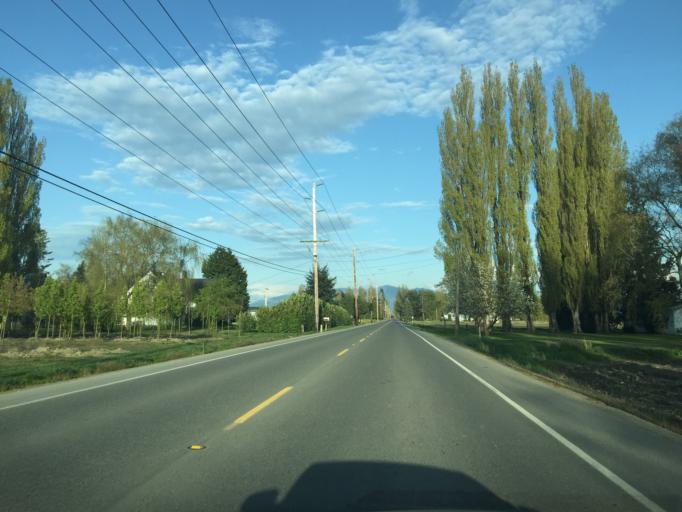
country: US
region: Washington
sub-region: Skagit County
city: Mount Vernon
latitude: 48.4208
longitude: -122.4188
